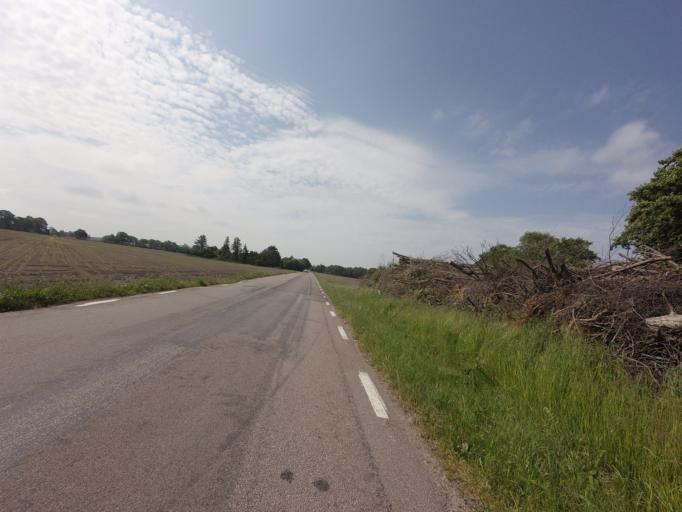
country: SE
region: Skane
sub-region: Helsingborg
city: Odakra
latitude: 56.2070
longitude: 12.7060
